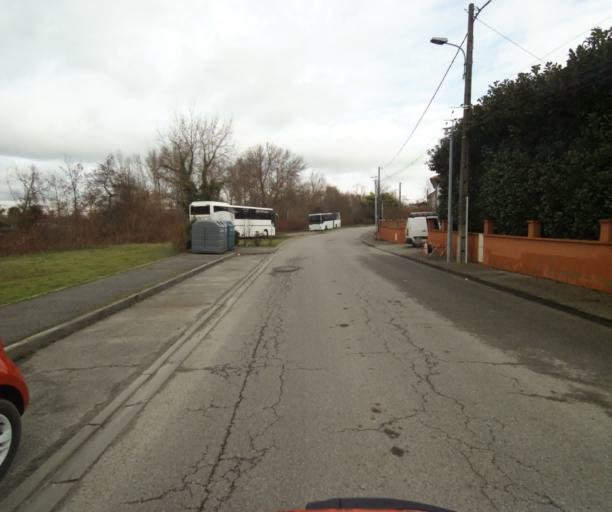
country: FR
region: Midi-Pyrenees
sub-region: Departement de l'Ariege
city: Pamiers
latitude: 43.1225
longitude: 1.6004
